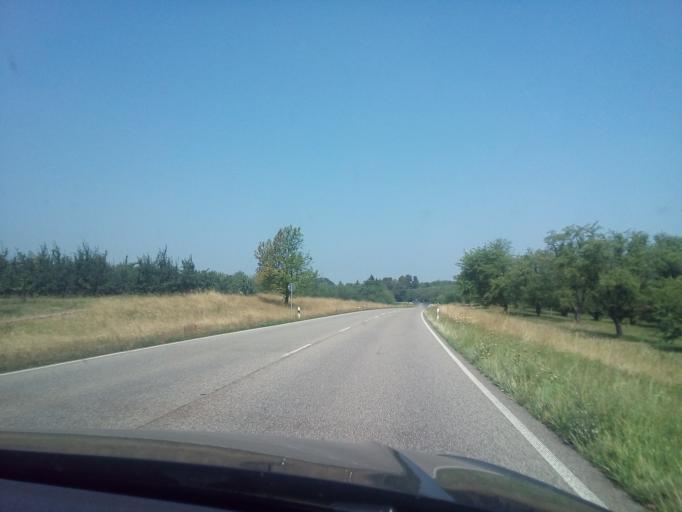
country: DE
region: Baden-Wuerttemberg
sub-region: Freiburg Region
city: Achern
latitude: 48.6146
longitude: 8.0686
